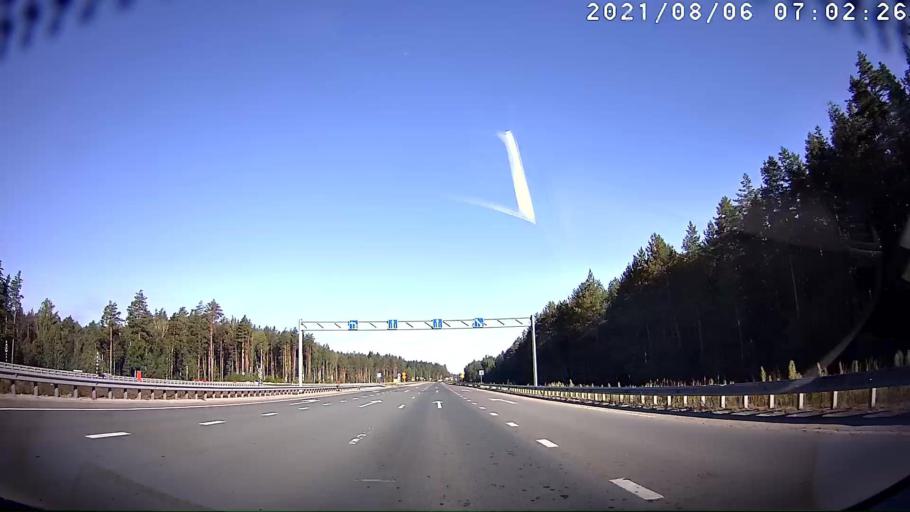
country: RU
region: Mariy-El
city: Yoshkar-Ola
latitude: 56.5341
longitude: 47.9965
